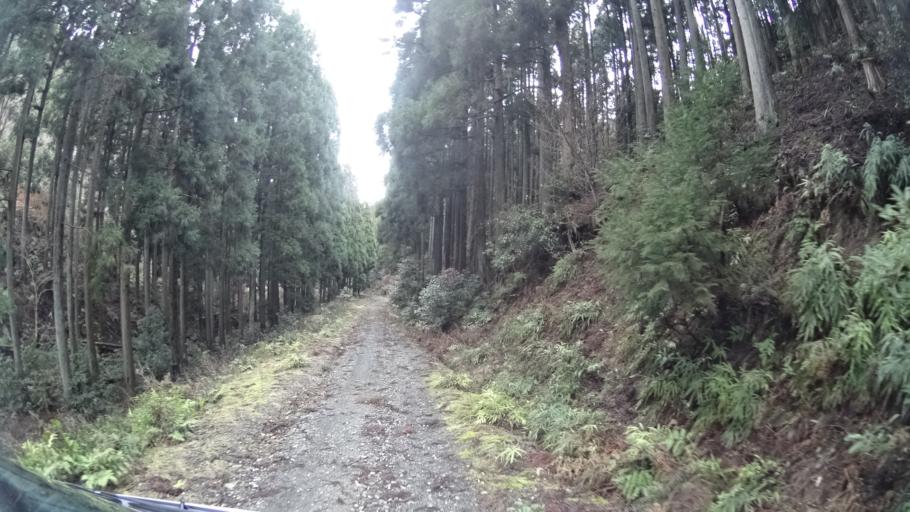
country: JP
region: Kyoto
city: Ayabe
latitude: 35.3105
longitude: 135.3767
